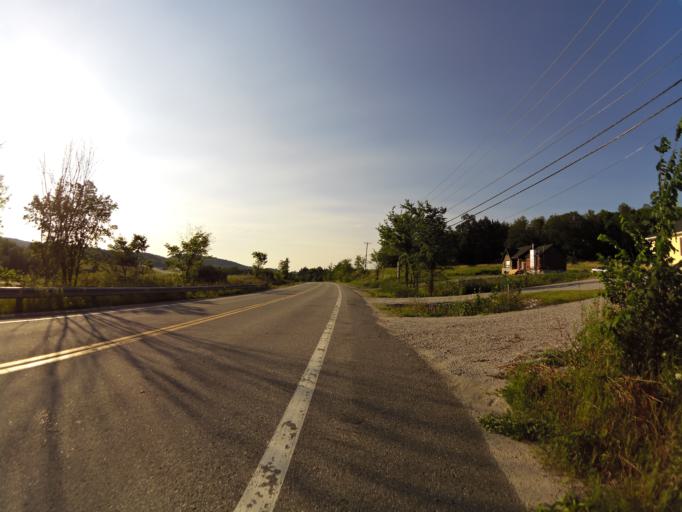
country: CA
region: Quebec
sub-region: Outaouais
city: Wakefield
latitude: 45.5931
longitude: -75.8923
